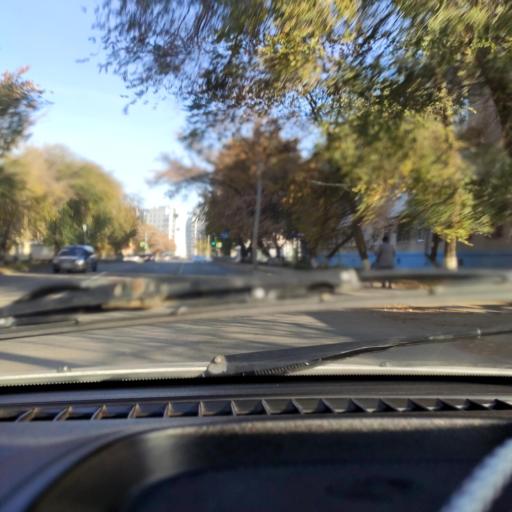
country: RU
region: Samara
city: Tol'yatti
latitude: 53.5187
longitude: 49.4143
